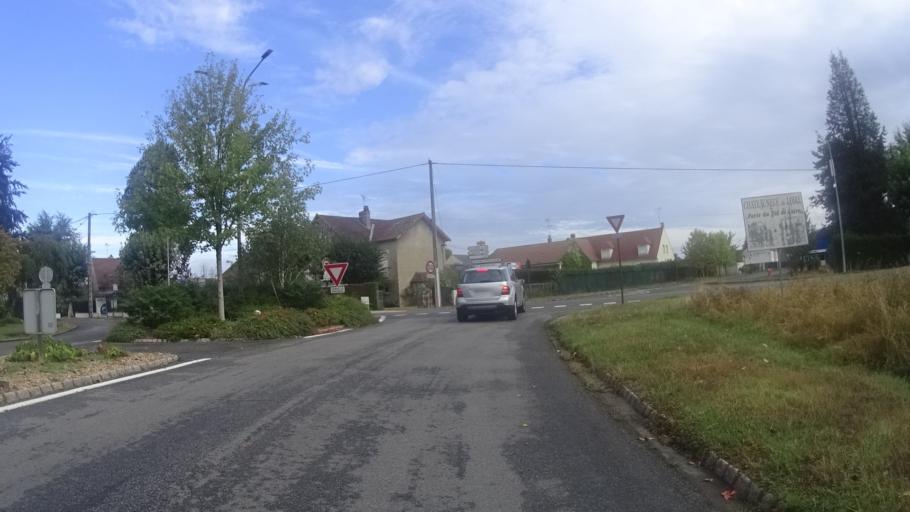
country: FR
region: Centre
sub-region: Departement du Loiret
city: Chateauneuf-sur-Loire
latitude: 47.8606
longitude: 2.2387
